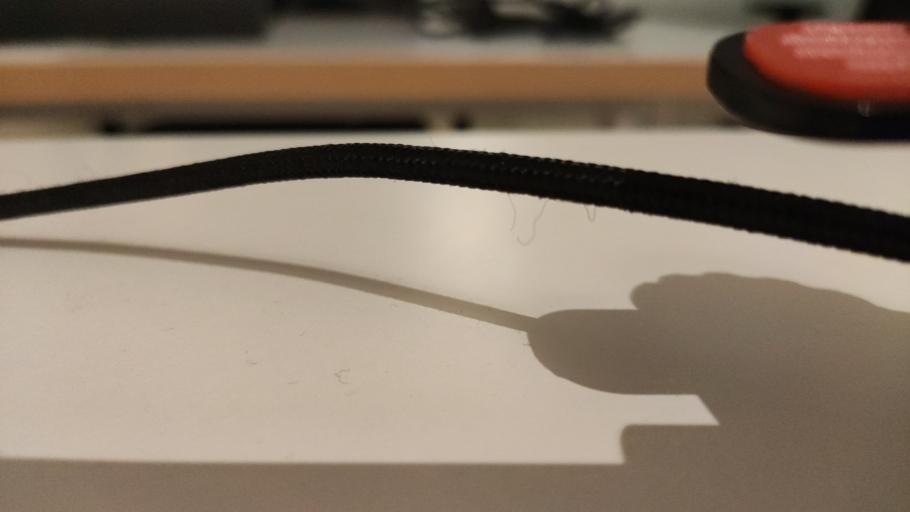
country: RU
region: Moskovskaya
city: Novoye
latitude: 55.6434
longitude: 38.9291
